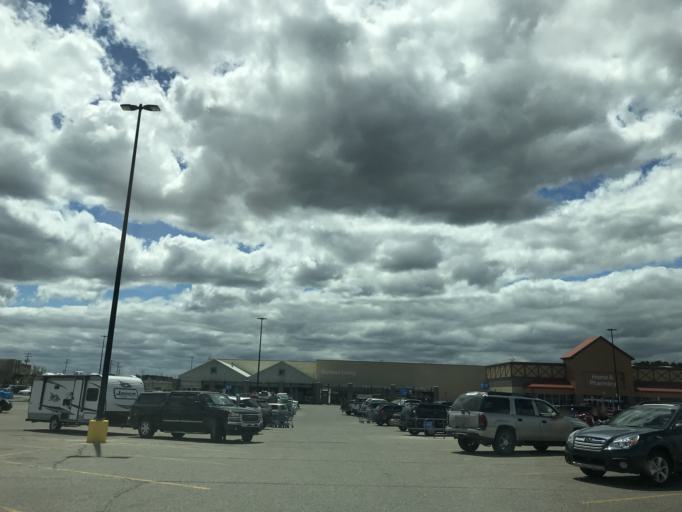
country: US
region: Michigan
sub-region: Otsego County
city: Gaylord
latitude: 45.0241
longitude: -84.6890
